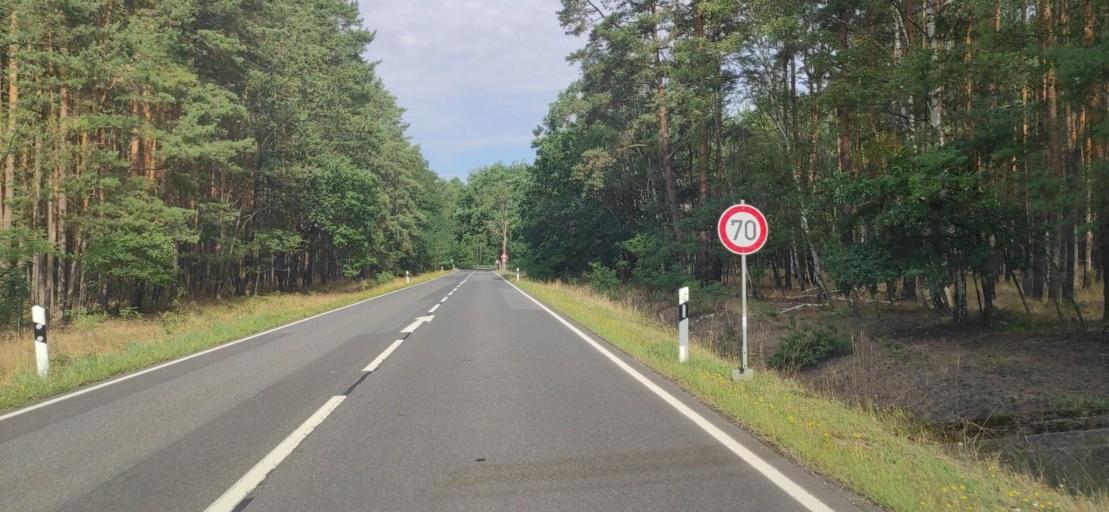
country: PL
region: Lubusz
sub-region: Powiat zarski
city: Trzebiel
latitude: 51.6738
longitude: 14.7329
